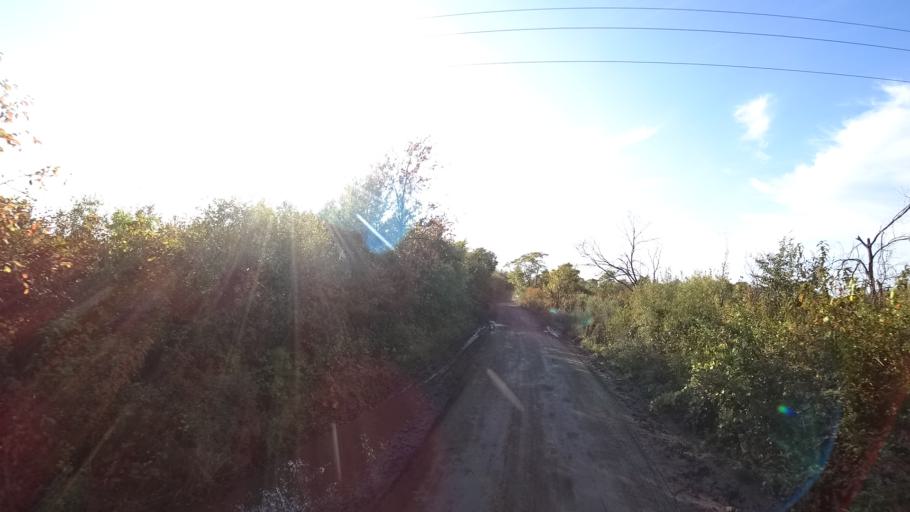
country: RU
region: Amur
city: Arkhara
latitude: 49.3561
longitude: 130.1282
